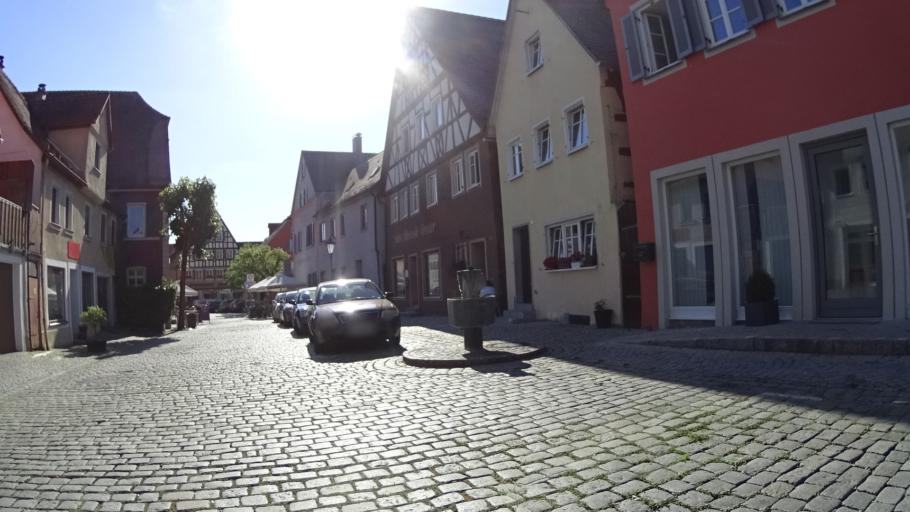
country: DE
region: Bavaria
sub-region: Regierungsbezirk Mittelfranken
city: Feuchtwangen
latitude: 49.1677
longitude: 10.3323
